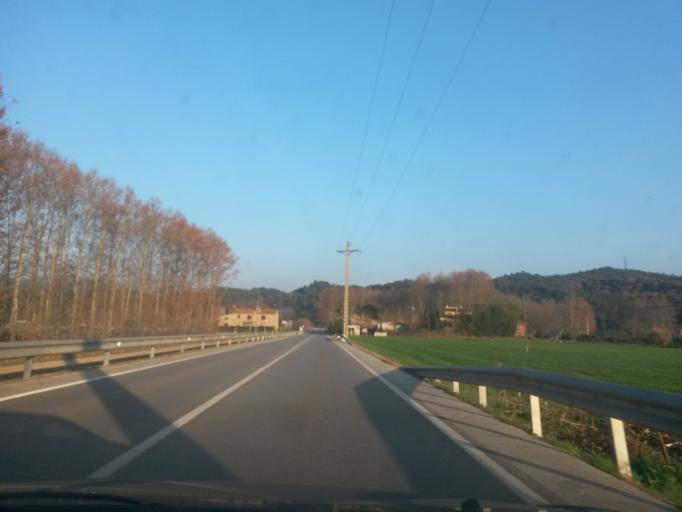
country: ES
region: Catalonia
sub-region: Provincia de Girona
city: Angles
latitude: 41.9614
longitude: 2.6628
